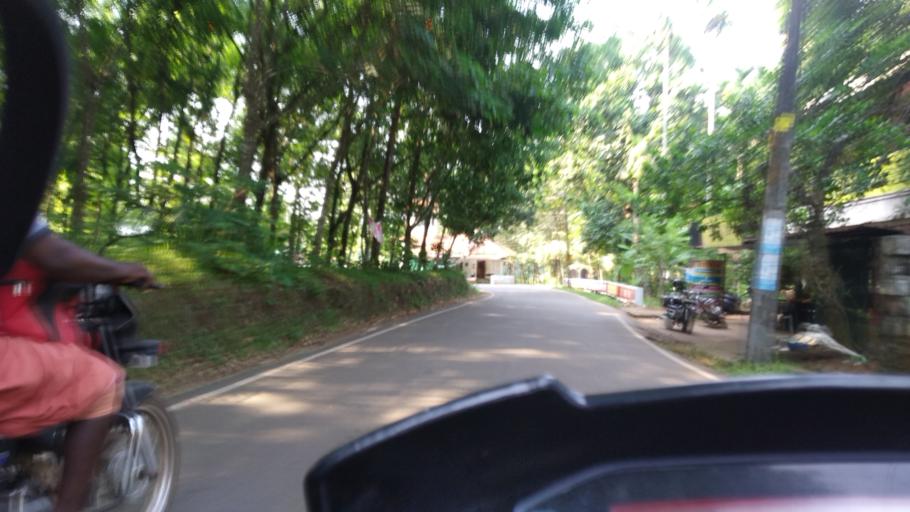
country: IN
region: Kerala
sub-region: Ernakulam
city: Piravam
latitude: 9.8581
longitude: 76.5201
